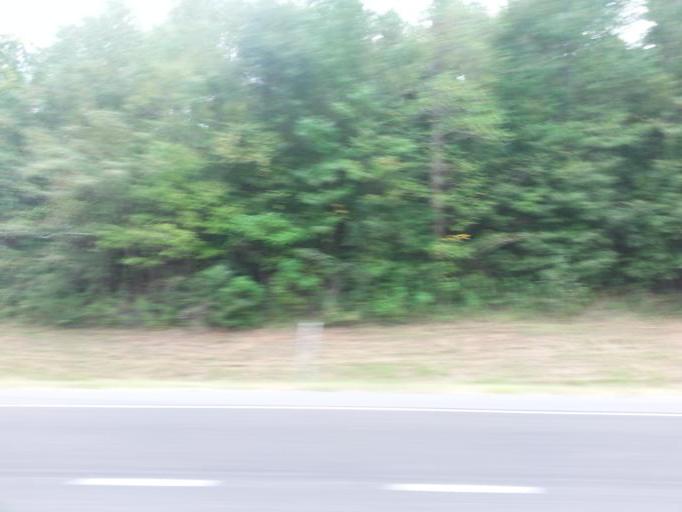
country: US
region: Alabama
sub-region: Conecuh County
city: Evergreen
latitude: 31.5030
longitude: -86.9259
